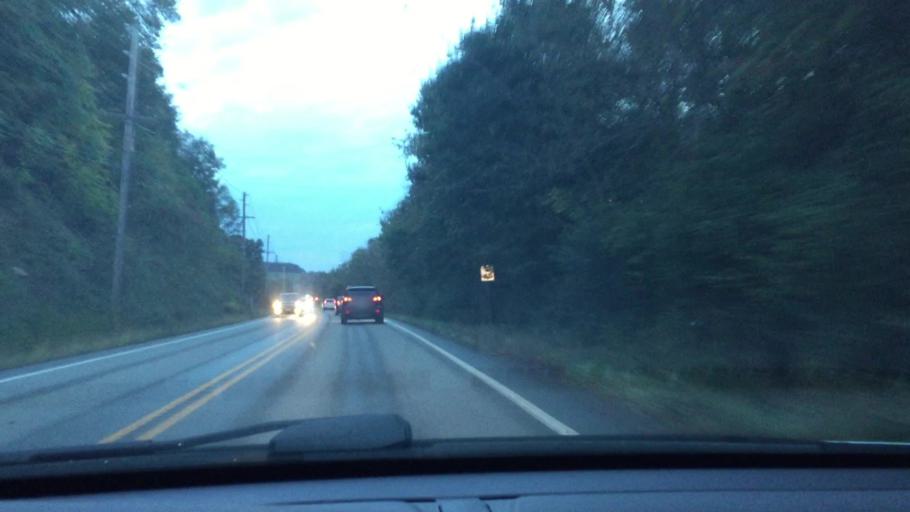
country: US
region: Pennsylvania
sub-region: Washington County
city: McGovern
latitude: 40.1832
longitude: -80.1399
